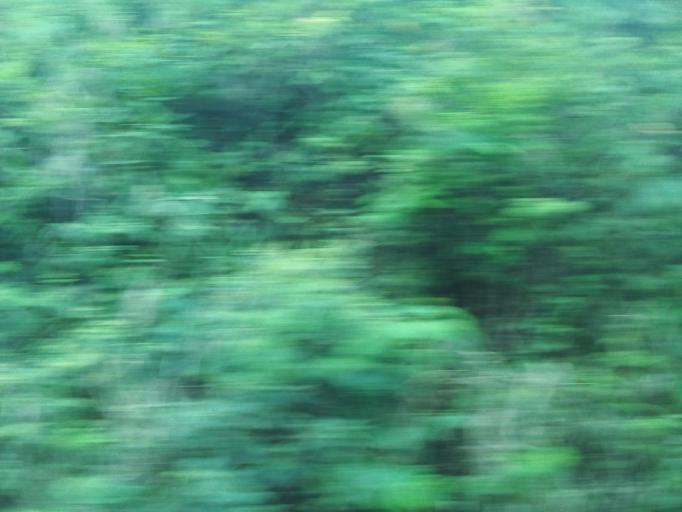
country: BR
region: Minas Gerais
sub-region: Joao Monlevade
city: Joao Monlevade
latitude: -19.8251
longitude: -43.1065
